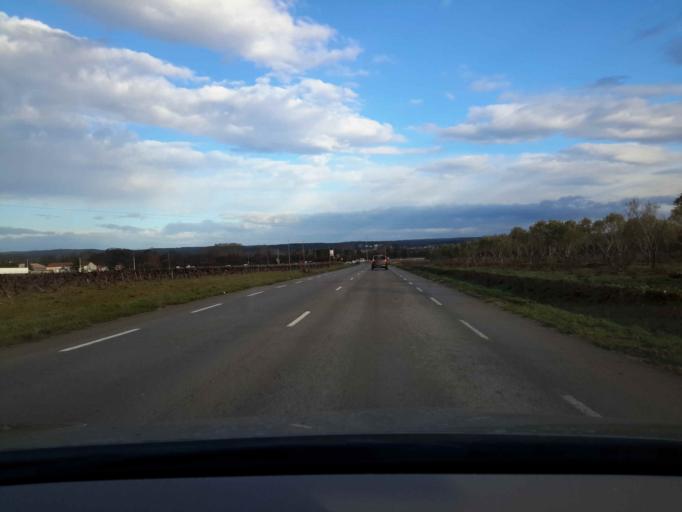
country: FR
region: Languedoc-Roussillon
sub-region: Departement du Gard
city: Aubord
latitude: 43.7666
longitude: 4.3296
